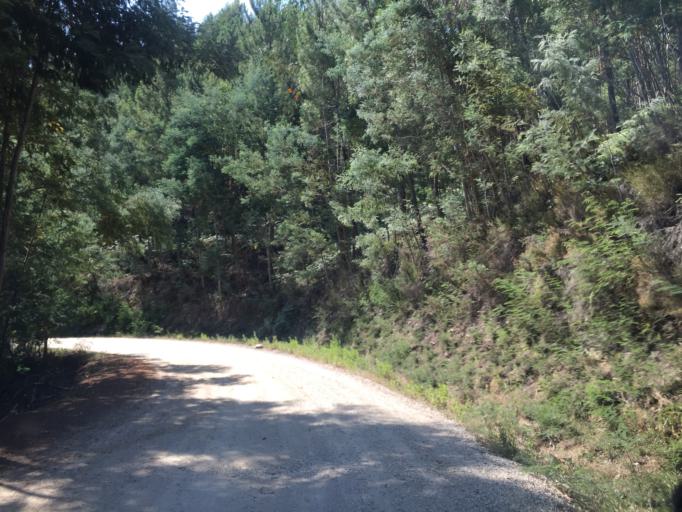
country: PT
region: Leiria
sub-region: Pedrogao Grande
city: Pedrogao Grande
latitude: 39.9295
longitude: -8.1247
